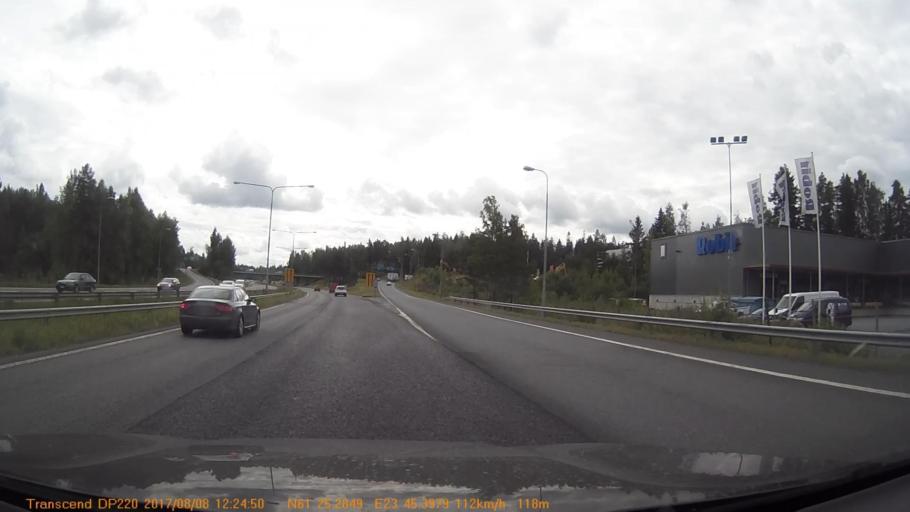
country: FI
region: Pirkanmaa
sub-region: Tampere
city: Tampere
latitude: 61.4212
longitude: 23.7568
